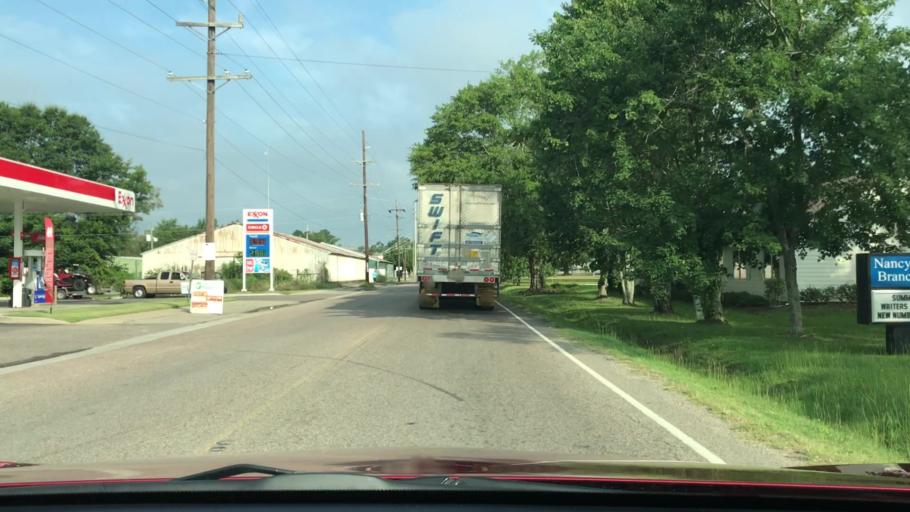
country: US
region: South Carolina
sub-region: Barnwell County
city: Williston
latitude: 33.6496
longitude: -81.3585
